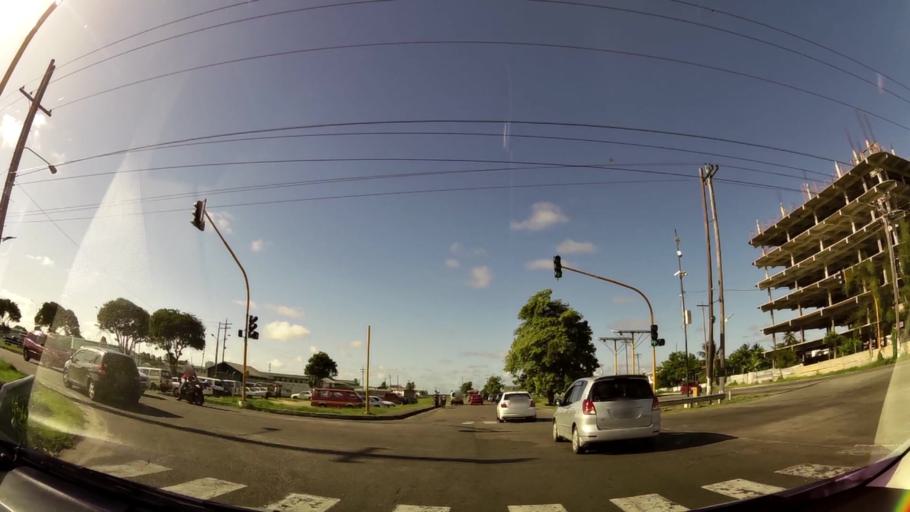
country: GY
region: Demerara-Mahaica
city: Georgetown
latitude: 6.8183
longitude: -58.1453
